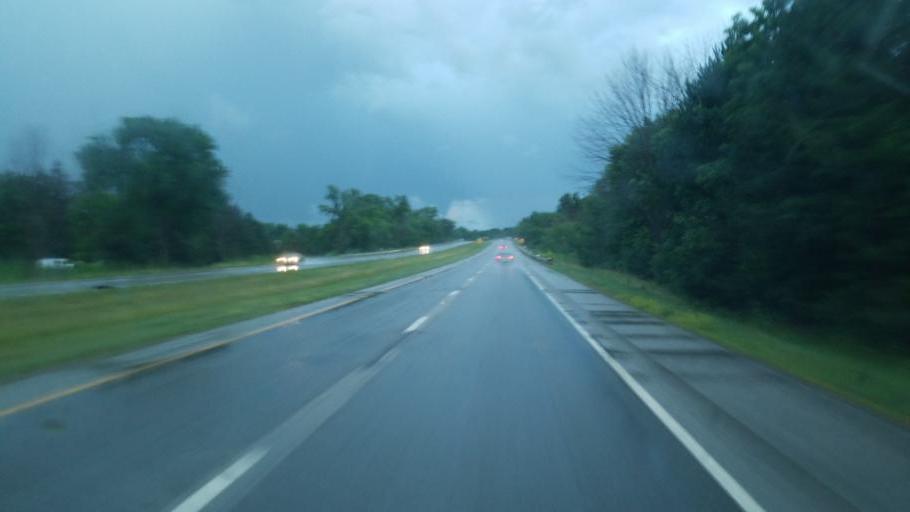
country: US
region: Ohio
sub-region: Summit County
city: Clinton
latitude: 40.9486
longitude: -81.6580
